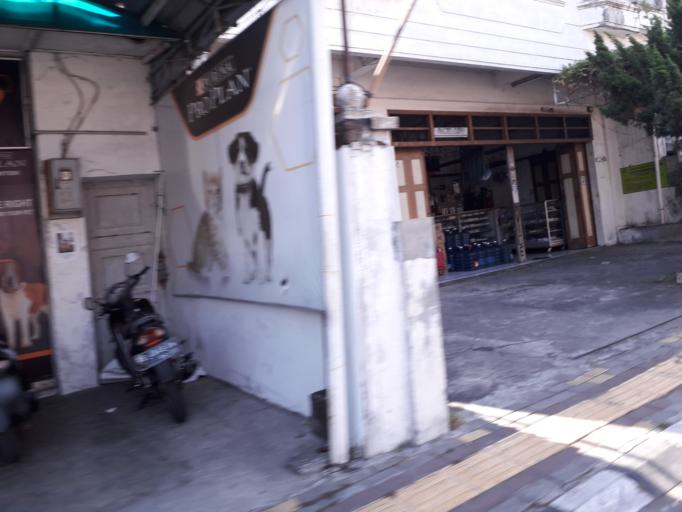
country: ID
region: Daerah Istimewa Yogyakarta
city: Yogyakarta
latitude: -7.7916
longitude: 110.3724
